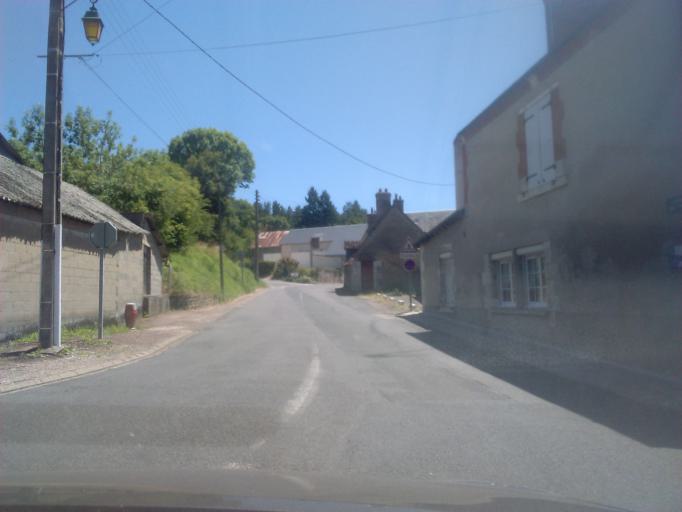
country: FR
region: Centre
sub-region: Departement du Loir-et-Cher
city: Saint-Sulpice-de-Pommeray
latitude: 47.5770
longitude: 1.2176
